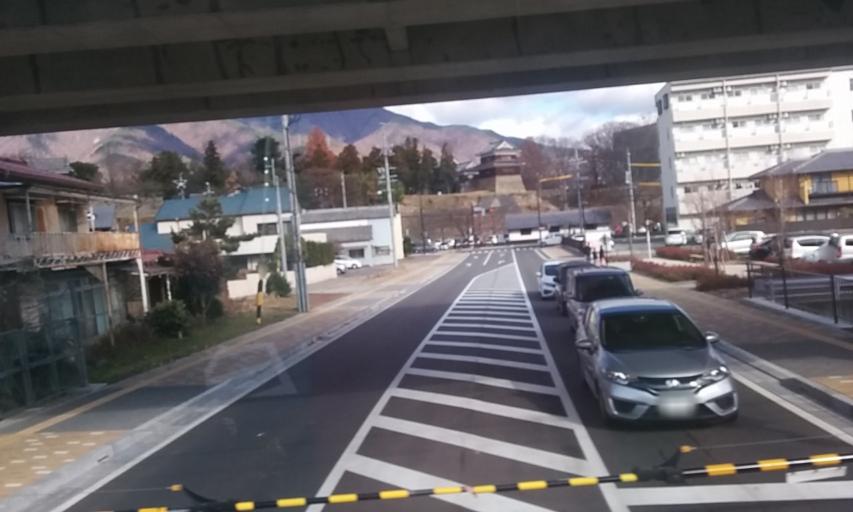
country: JP
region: Nagano
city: Ueda
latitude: 36.4014
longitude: 138.2432
